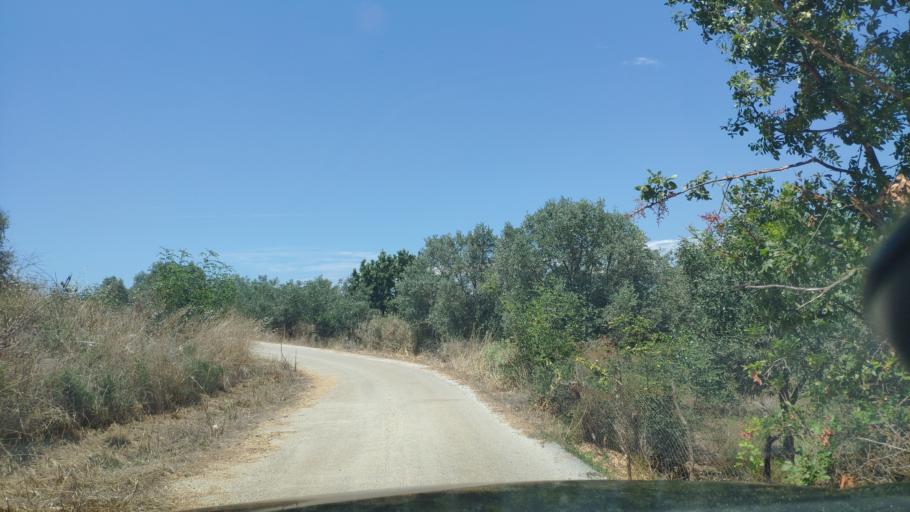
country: GR
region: West Greece
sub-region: Nomos Aitolias kai Akarnanias
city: Amfilochia
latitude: 38.9073
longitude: 21.1031
